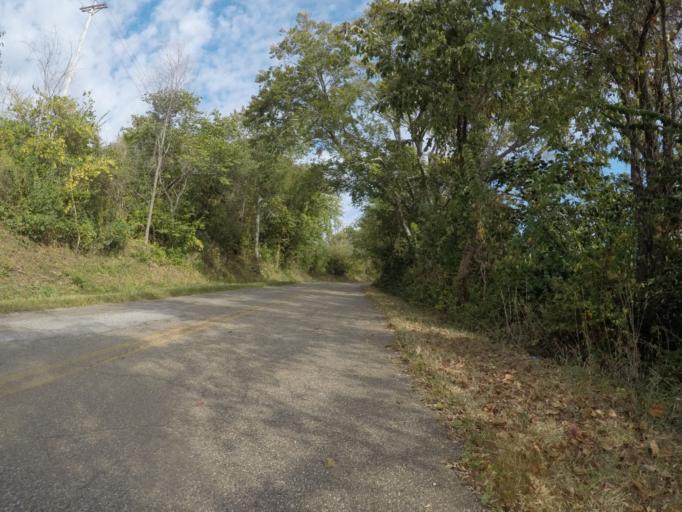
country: US
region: West Virginia
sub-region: Cabell County
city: Lesage
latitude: 38.5638
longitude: -82.4275
